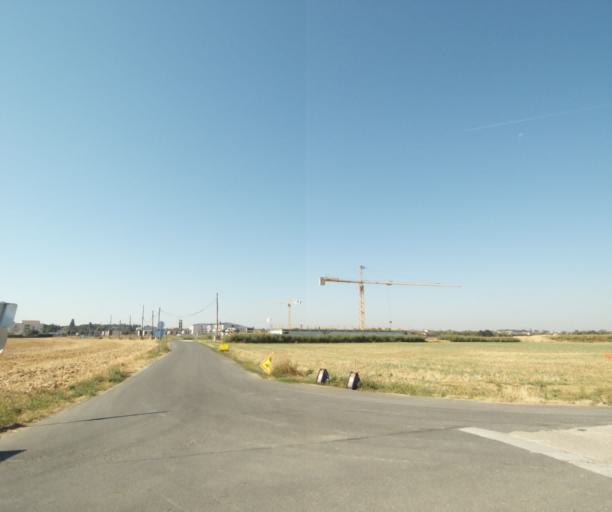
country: FR
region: Ile-de-France
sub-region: Departement de Seine-et-Marne
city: Moissy-Cramayel
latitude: 48.6368
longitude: 2.5866
